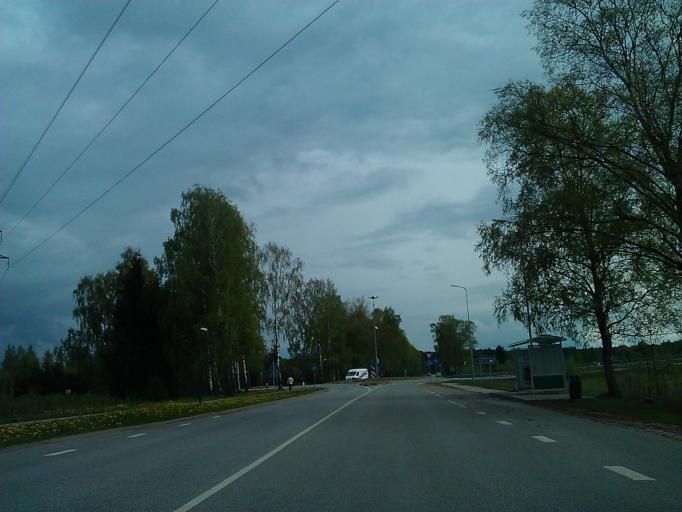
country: LV
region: Adazi
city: Adazi
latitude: 57.0696
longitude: 24.3217
